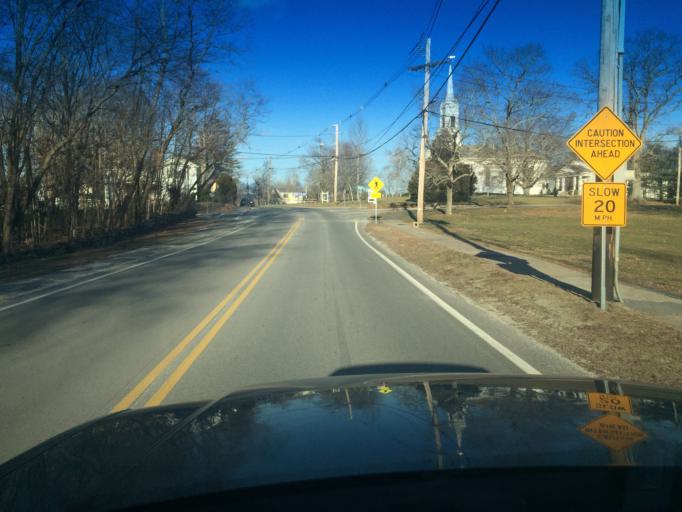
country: US
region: Massachusetts
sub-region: Middlesex County
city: Sherborn
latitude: 42.2401
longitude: -71.3717
